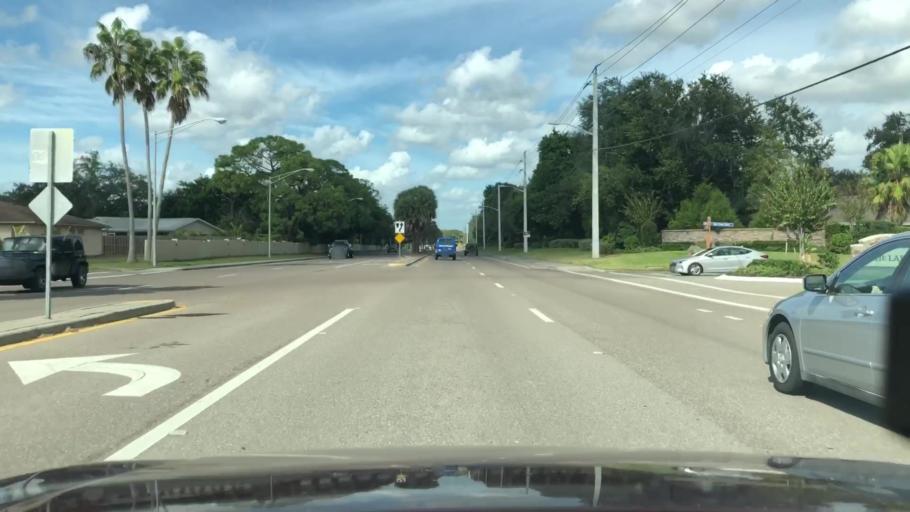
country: US
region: Florida
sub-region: Sarasota County
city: Sarasota Springs
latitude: 27.3182
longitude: -82.4828
